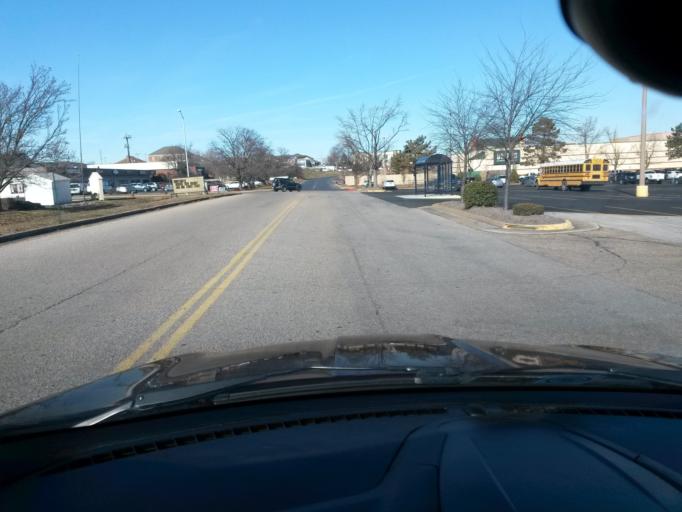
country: US
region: Virginia
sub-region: Rockingham County
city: Massanetta Springs
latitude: 38.4270
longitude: -78.8451
